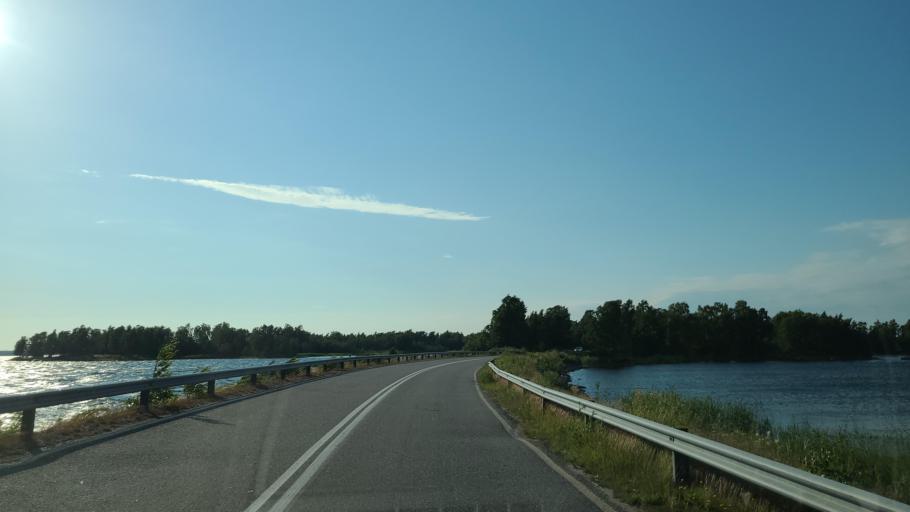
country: FI
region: Ostrobothnia
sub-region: Vaasa
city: Replot
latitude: 63.2816
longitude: 21.3381
